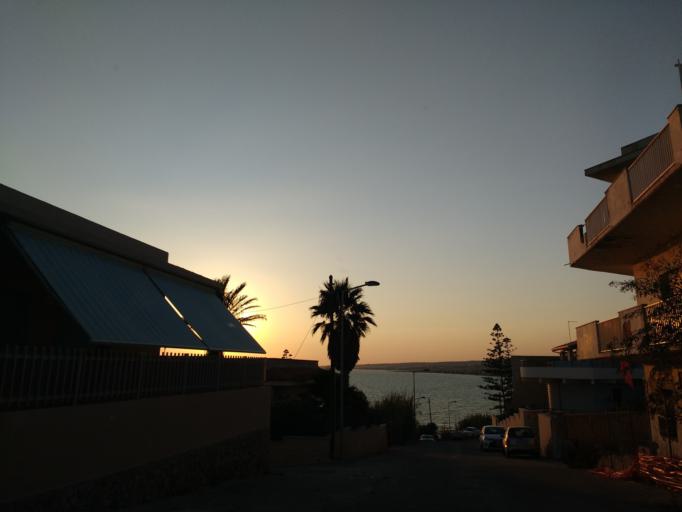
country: IT
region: Sicily
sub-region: Ragusa
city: Cava d'Aliga
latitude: 36.7311
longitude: 14.6822
